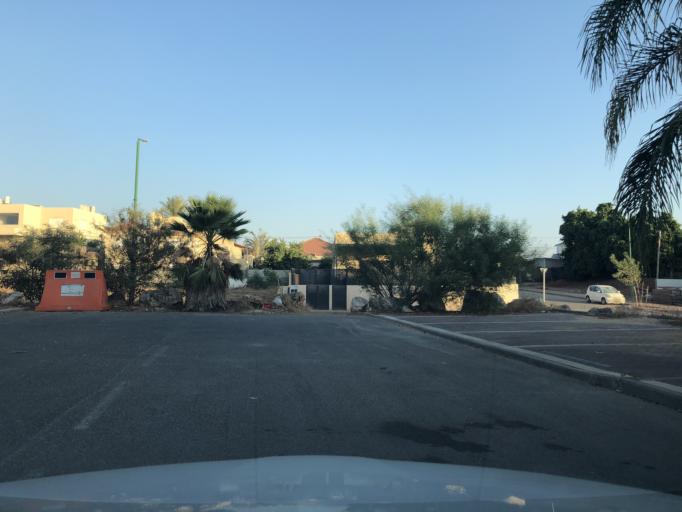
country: PS
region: West Bank
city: Hablah
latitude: 32.1587
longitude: 34.9712
